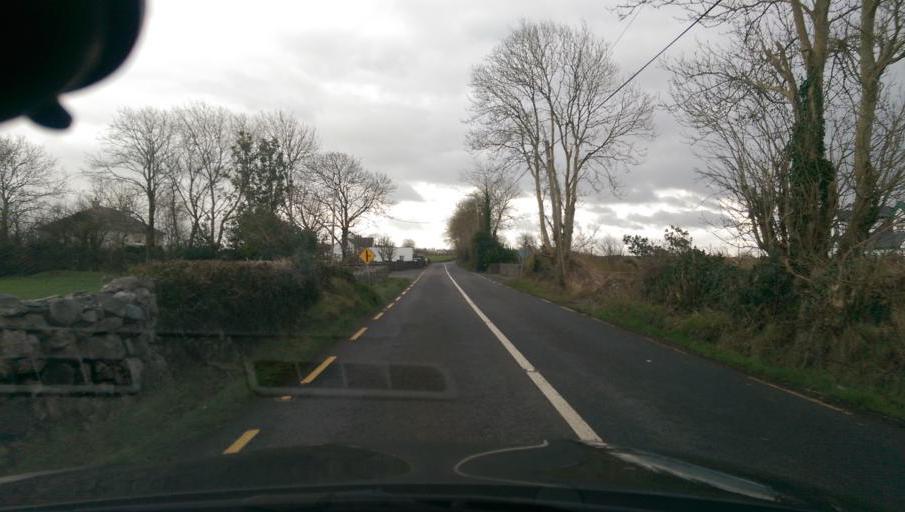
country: IE
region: Connaught
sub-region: County Galway
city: Athenry
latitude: 53.3146
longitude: -8.8079
